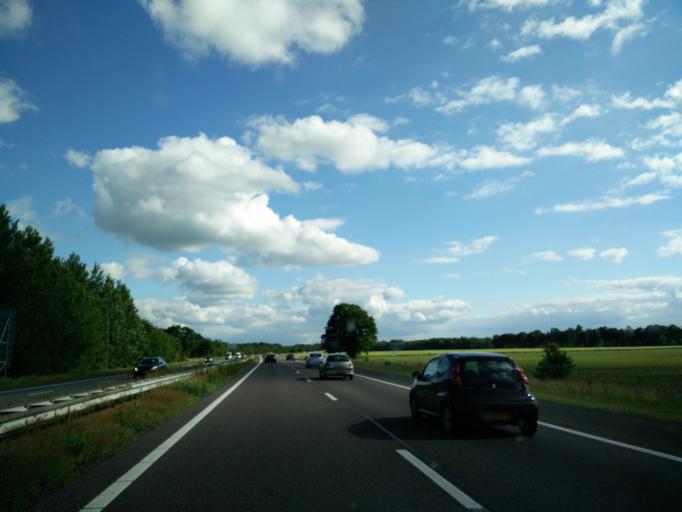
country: NL
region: Drenthe
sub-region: Gemeente Tynaarlo
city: Tynaarlo
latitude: 53.0734
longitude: 6.6034
